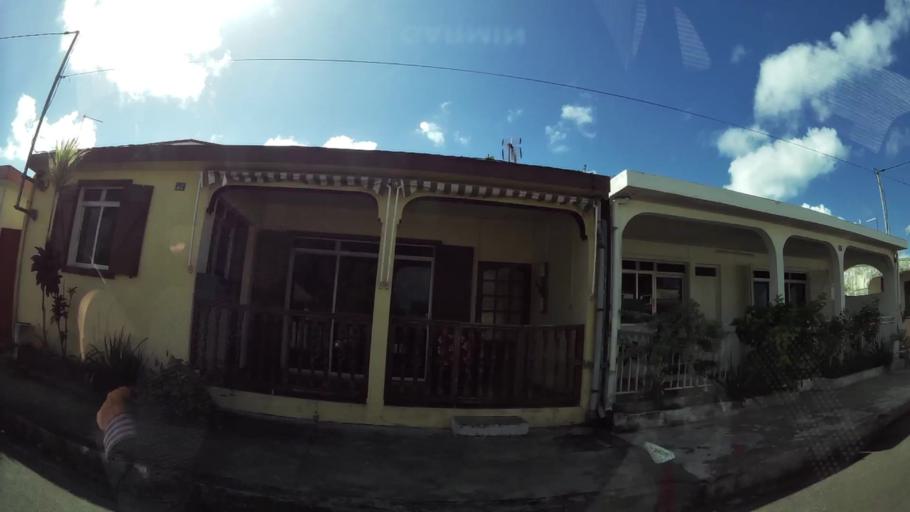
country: GP
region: Guadeloupe
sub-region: Guadeloupe
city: Port-Louis
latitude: 16.4200
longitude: -61.5323
